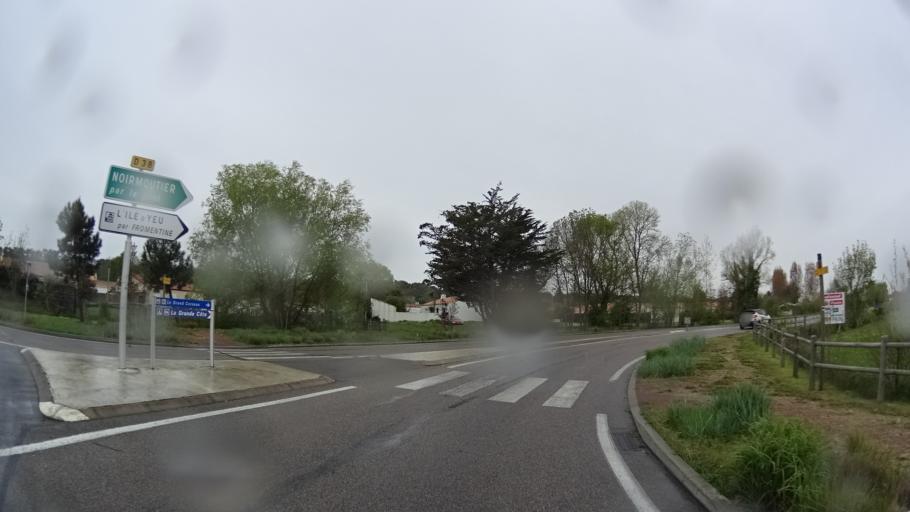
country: FR
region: Pays de la Loire
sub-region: Departement de la Vendee
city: La Barre-de-Monts
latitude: 46.8790
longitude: -2.1202
